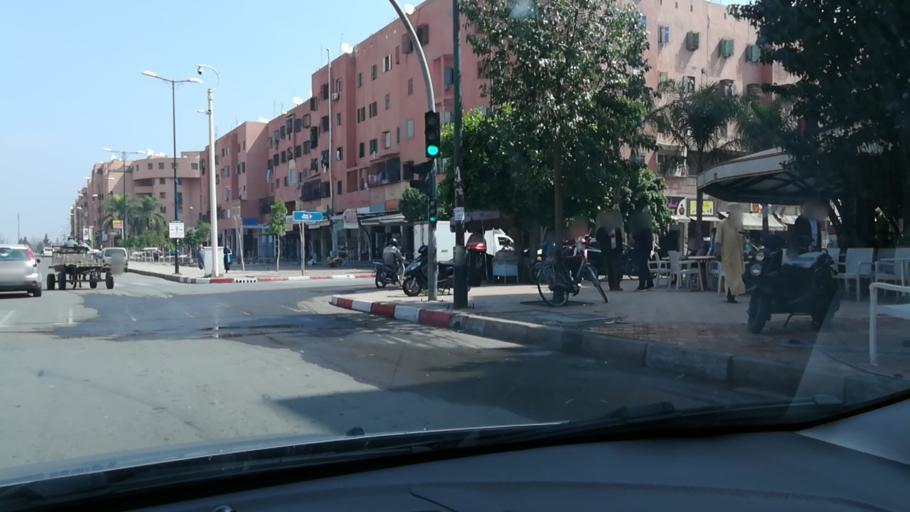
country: MA
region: Marrakech-Tensift-Al Haouz
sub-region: Marrakech
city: Marrakesh
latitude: 31.6333
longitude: -8.0583
